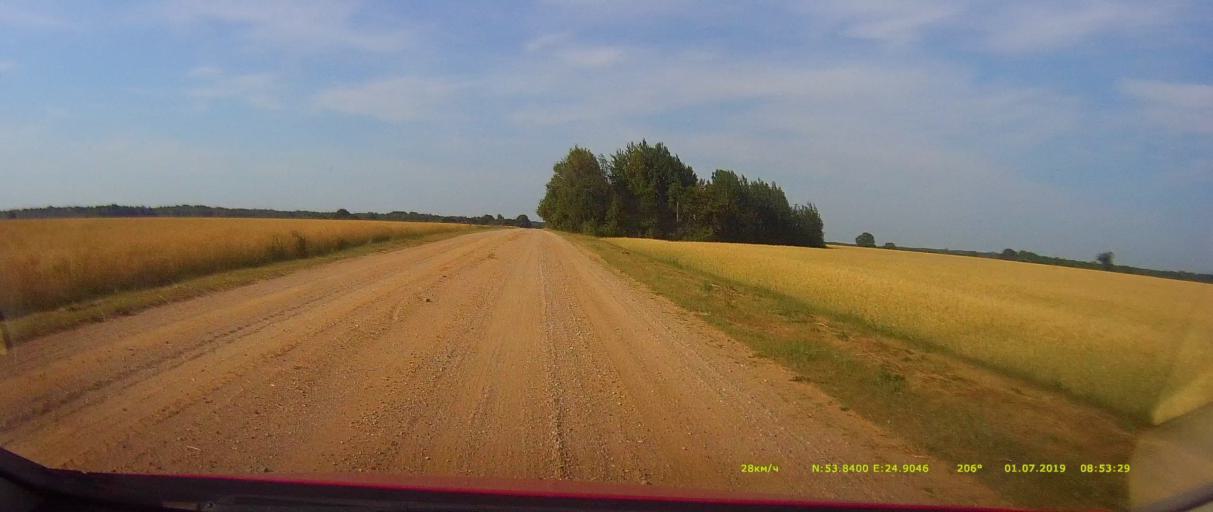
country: BY
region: Grodnenskaya
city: Shchuchin
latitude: 53.8401
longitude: 24.9047
